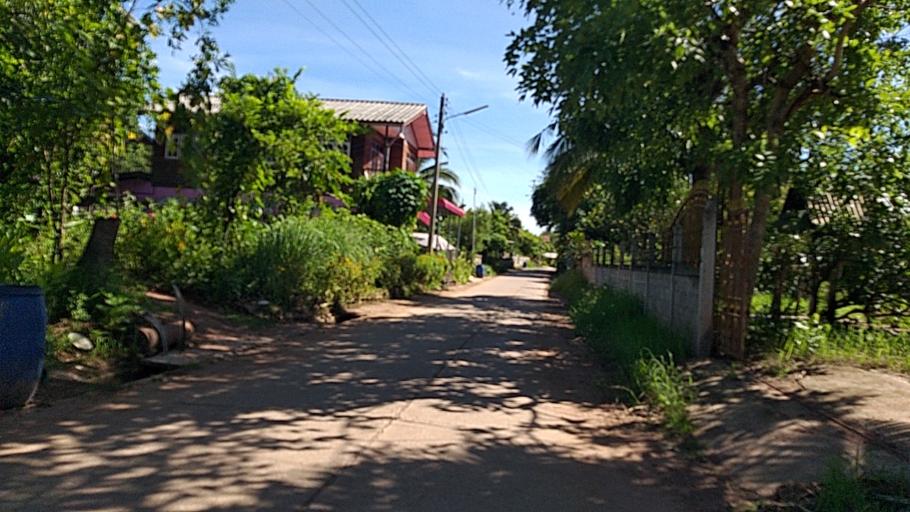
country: TH
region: Chaiyaphum
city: Ban Thaen
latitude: 16.4071
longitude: 102.3545
